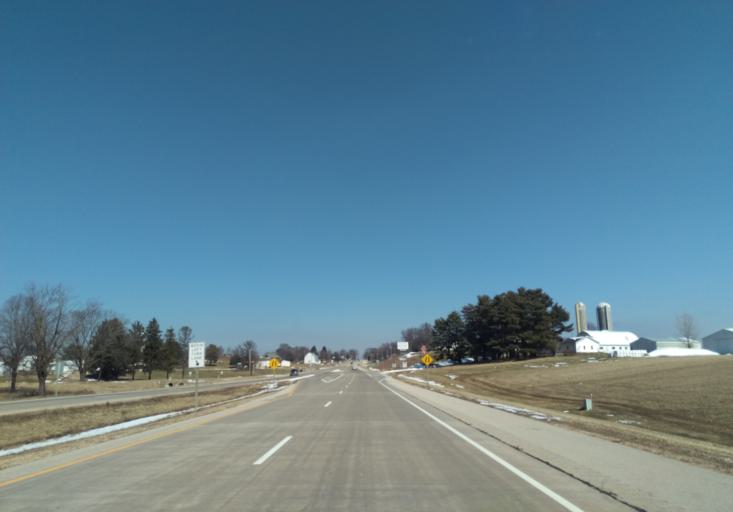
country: US
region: Wisconsin
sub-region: Vernon County
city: Westby
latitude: 43.6374
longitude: -90.8678
